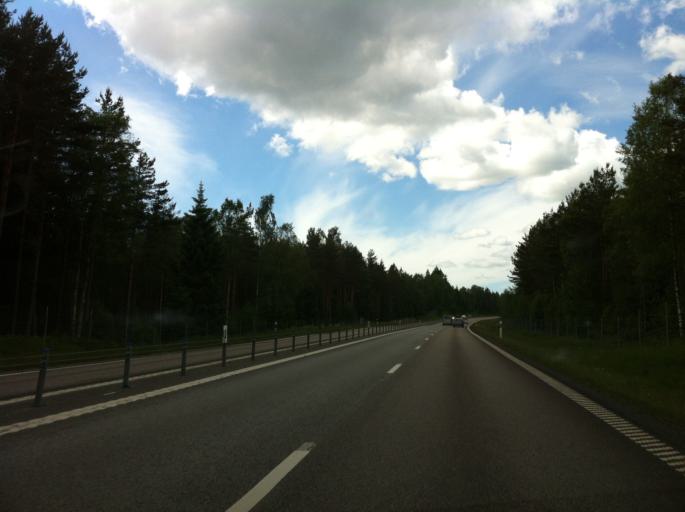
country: SE
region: Vaestra Goetaland
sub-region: Amals Kommun
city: Amal
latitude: 59.1014
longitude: 12.7836
